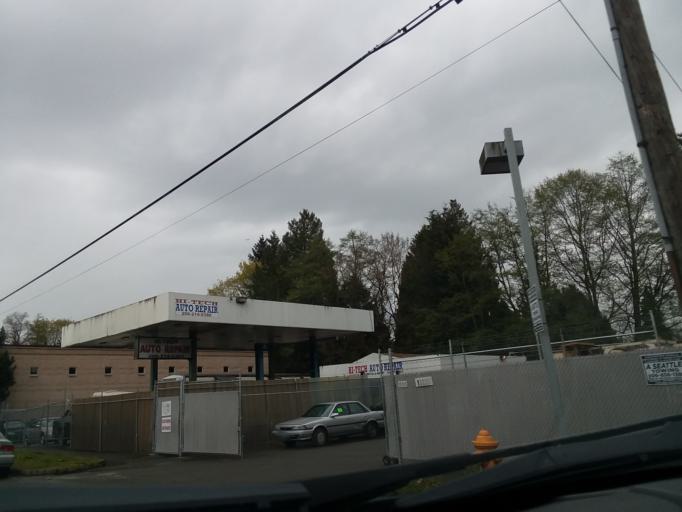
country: US
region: Washington
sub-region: King County
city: Burien
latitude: 47.4840
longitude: -122.3337
